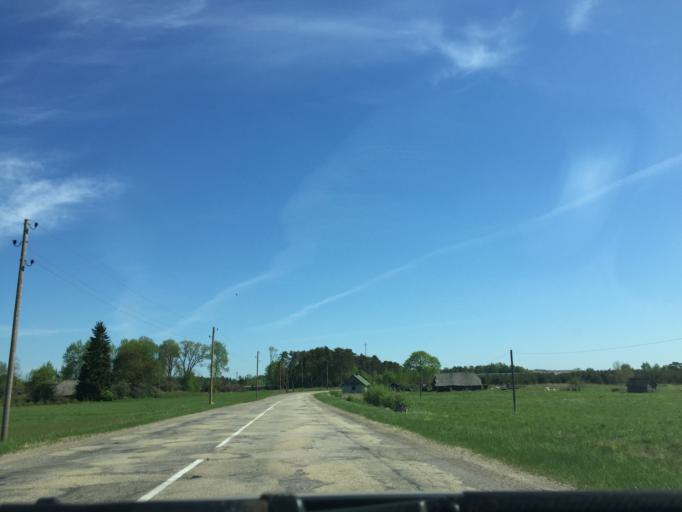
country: LV
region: Ropazu
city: Ropazi
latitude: 57.0159
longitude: 24.6086
